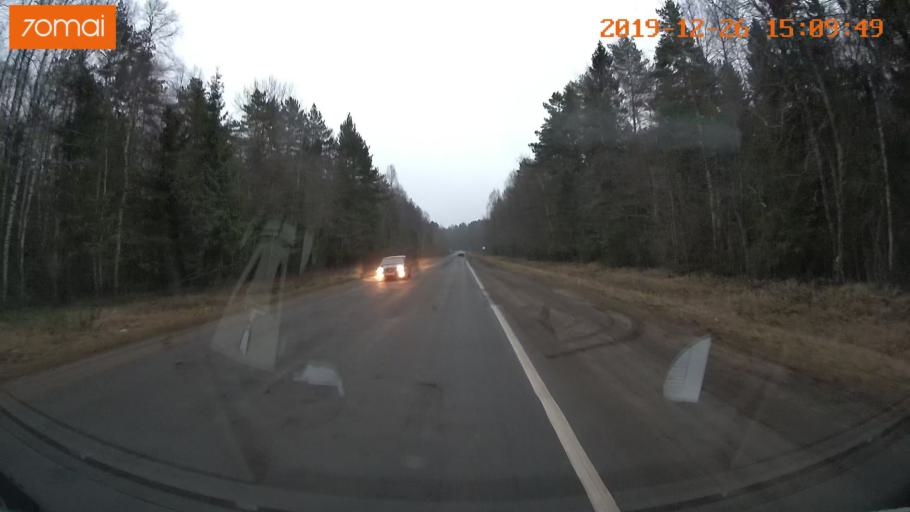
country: RU
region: Jaroslavl
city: Rybinsk
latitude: 58.1458
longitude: 38.8446
